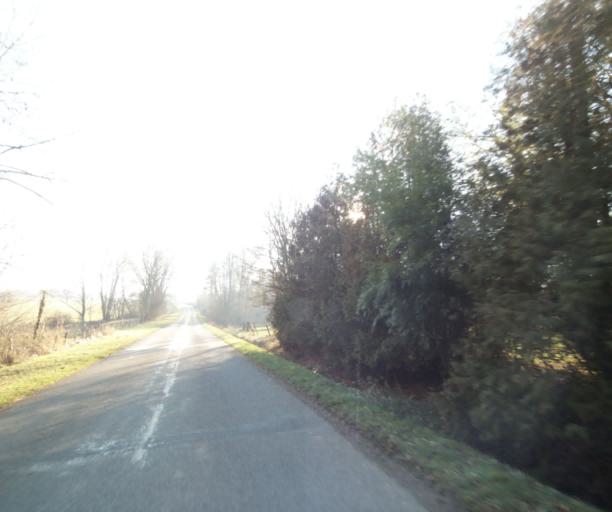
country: FR
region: Champagne-Ardenne
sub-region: Departement de la Haute-Marne
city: Bienville
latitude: 48.5976
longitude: 5.0805
